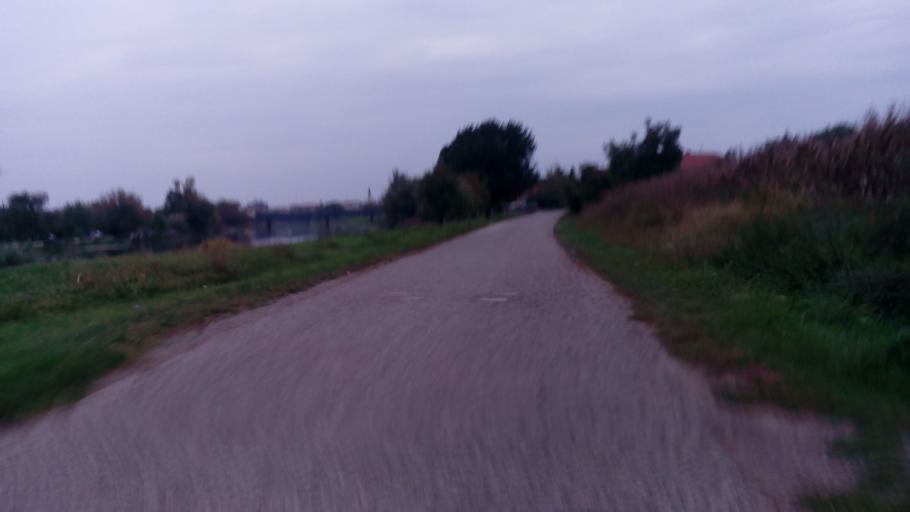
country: HR
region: Vukovarsko-Srijemska
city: Vinkovci
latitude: 45.2768
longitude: 18.8095
